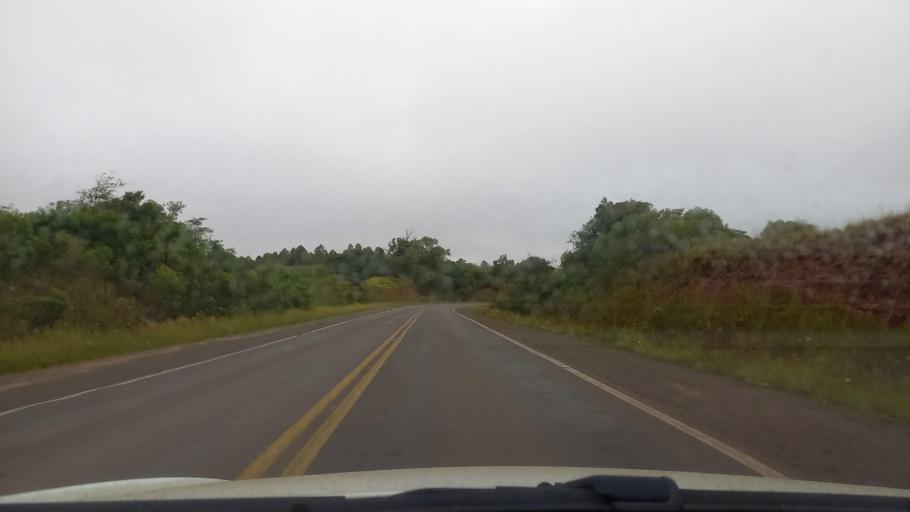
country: BR
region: Rio Grande do Sul
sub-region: Cacequi
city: Cacequi
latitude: -30.0983
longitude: -54.6300
